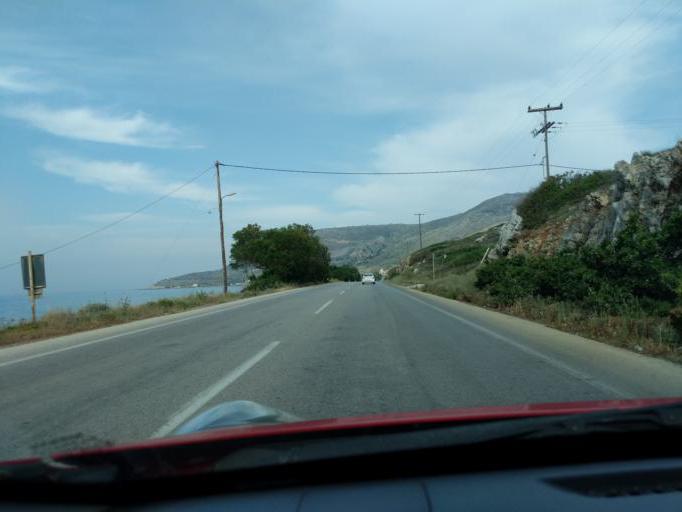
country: GR
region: Crete
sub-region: Nomos Chanias
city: Georgioupolis
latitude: 35.3504
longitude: 24.3465
